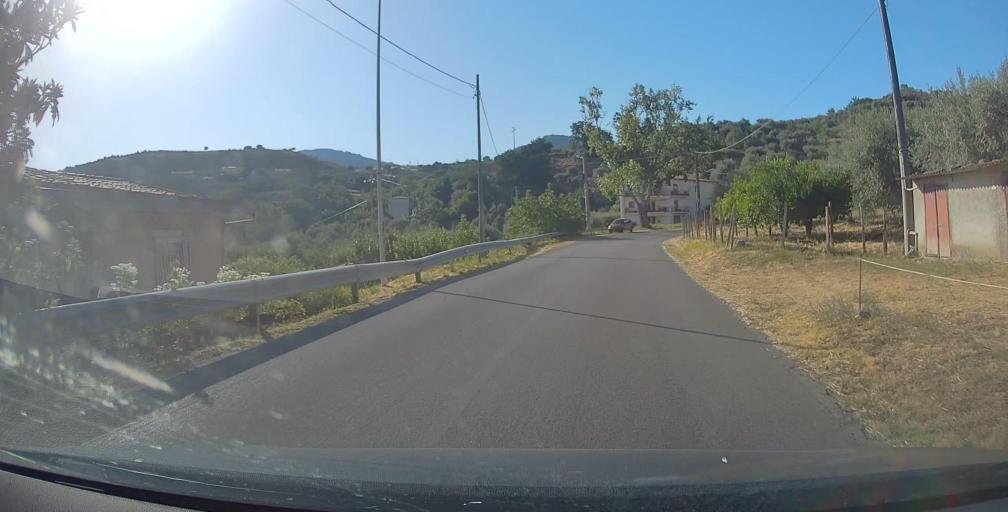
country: IT
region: Sicily
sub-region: Messina
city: Librizzi
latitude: 38.0775
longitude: 14.9760
